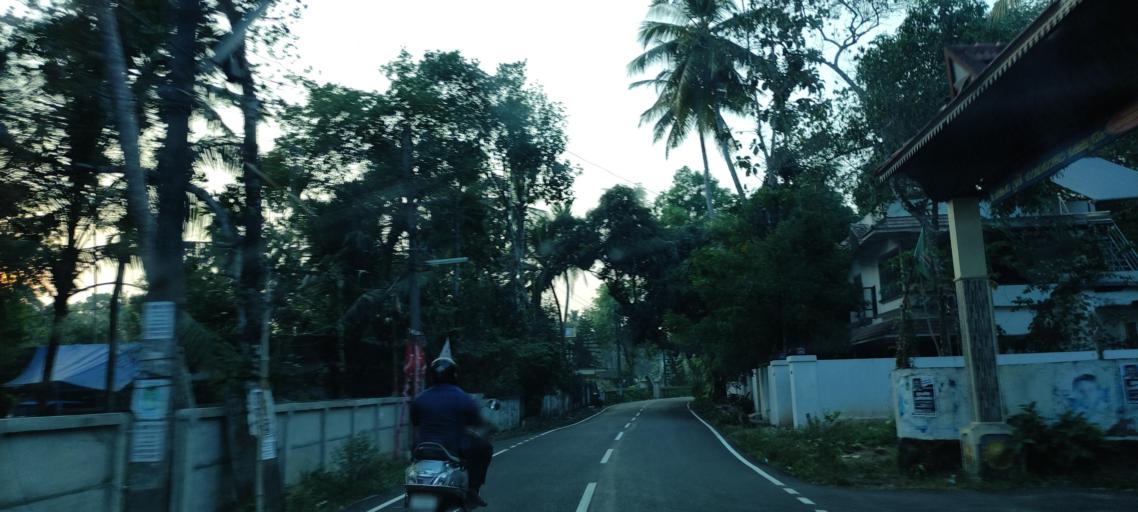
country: IN
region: Kerala
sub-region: Alappuzha
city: Mavelikara
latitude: 9.2677
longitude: 76.5441
